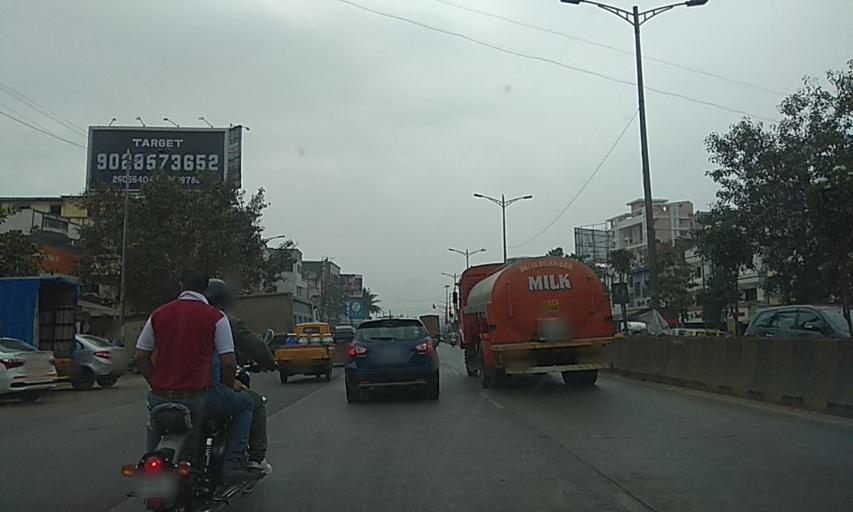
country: IN
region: Maharashtra
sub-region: Pune Division
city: Lohogaon
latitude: 18.5409
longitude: 73.9349
